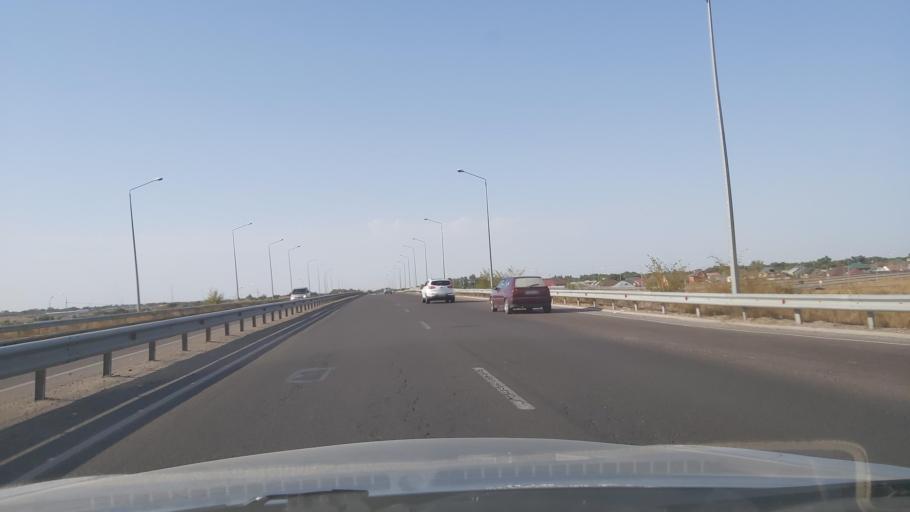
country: KZ
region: Almaty Oblysy
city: Energeticheskiy
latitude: 43.4675
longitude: 77.0327
